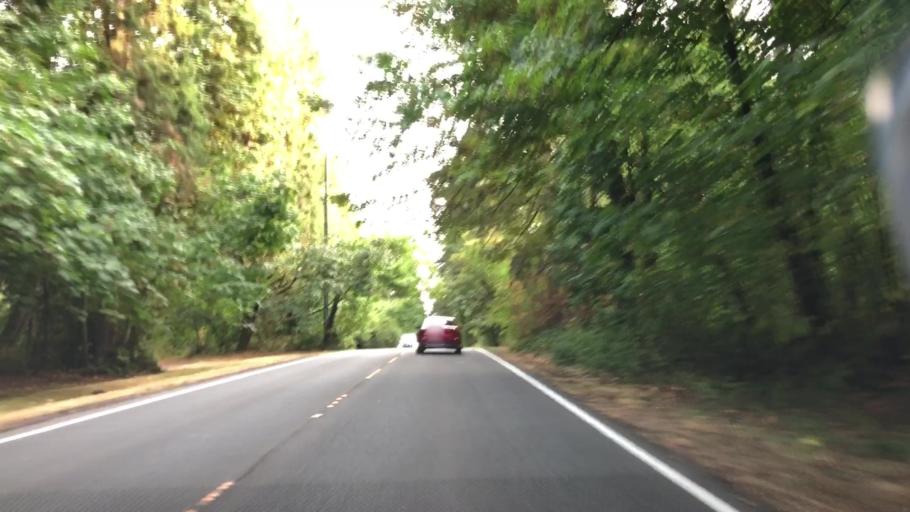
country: US
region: Washington
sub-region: King County
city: Mercer Island
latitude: 47.5444
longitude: -122.2216
